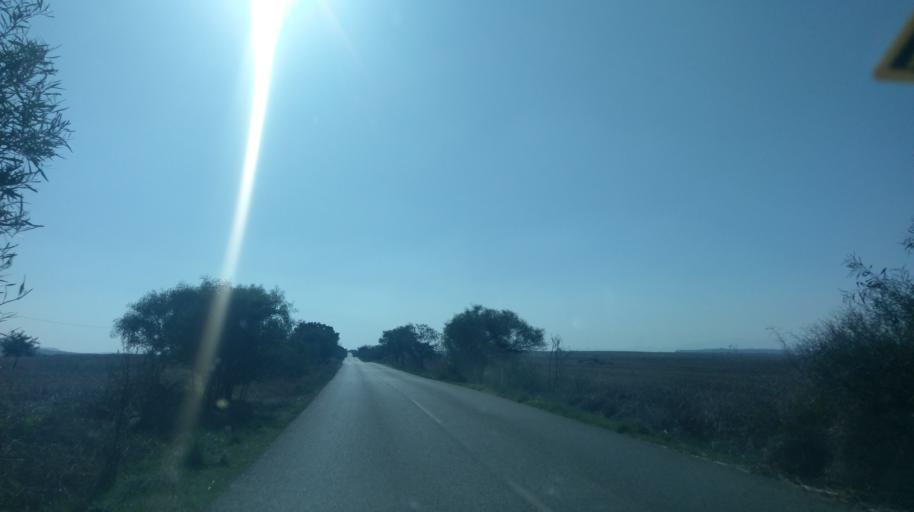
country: CY
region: Larnaka
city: Athienou
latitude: 35.1139
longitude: 33.4999
